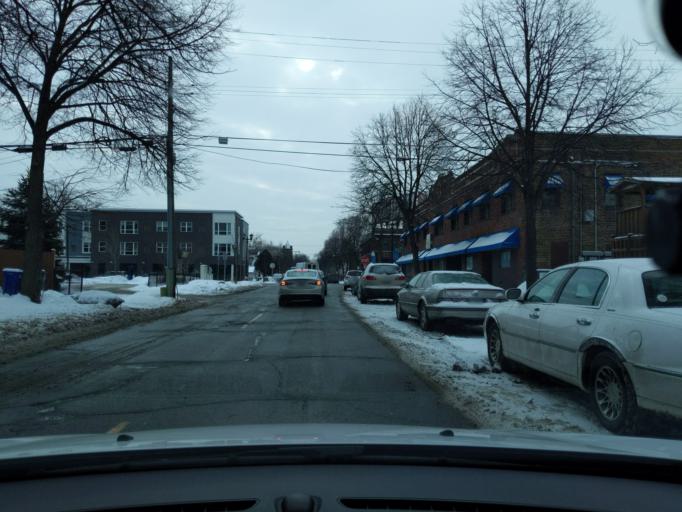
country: US
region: Minnesota
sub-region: Ramsey County
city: Saint Paul
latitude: 44.9472
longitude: -93.1365
